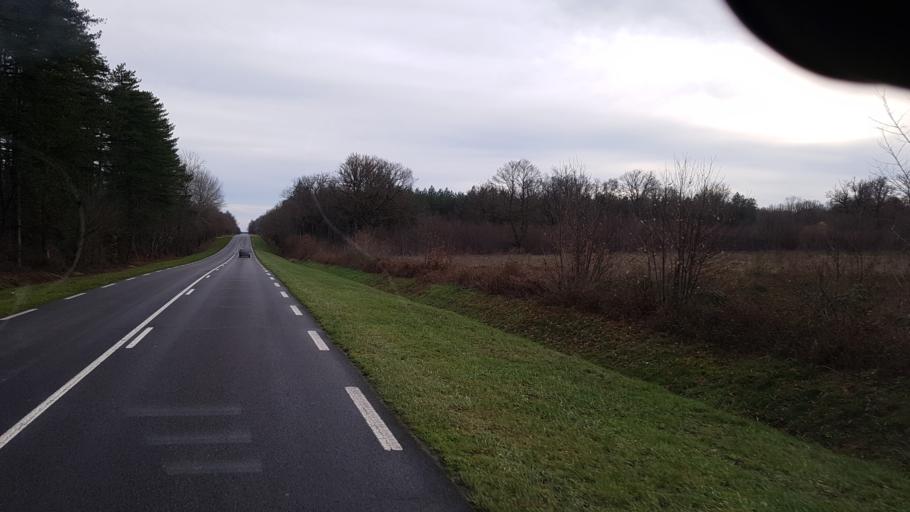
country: FR
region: Centre
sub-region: Departement du Loir-et-Cher
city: Lamotte-Beuvron
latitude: 47.6262
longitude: 2.0085
